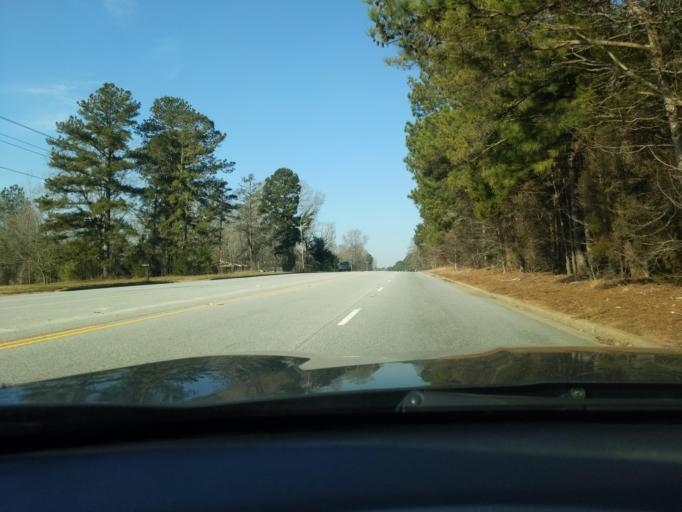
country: US
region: South Carolina
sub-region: Abbeville County
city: Abbeville
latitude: 34.1860
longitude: -82.3415
